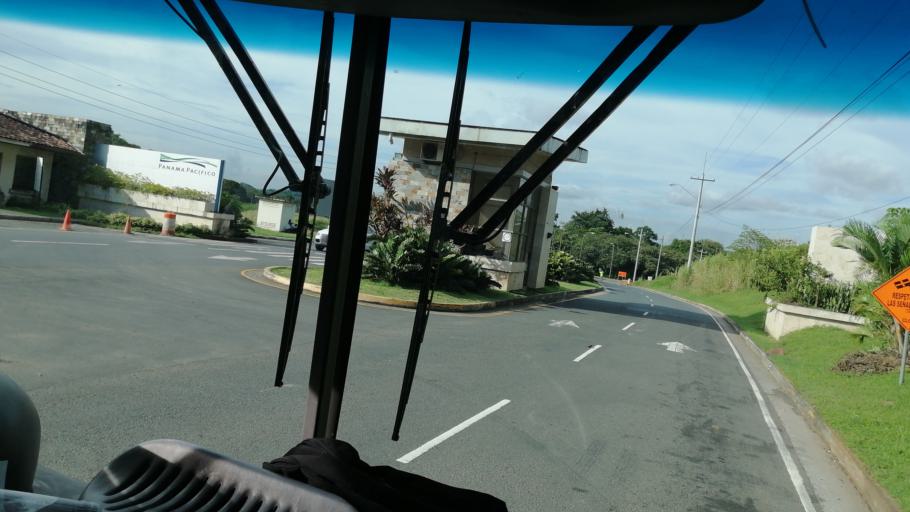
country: PA
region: Panama
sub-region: Distrito de Panama
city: Ancon
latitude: 8.9499
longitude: -79.5898
